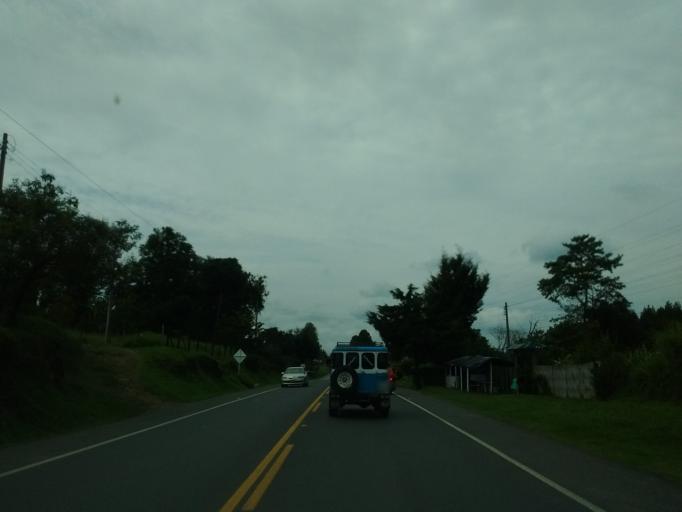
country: CO
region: Cauca
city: Cajibio
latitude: 2.5784
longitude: -76.5504
